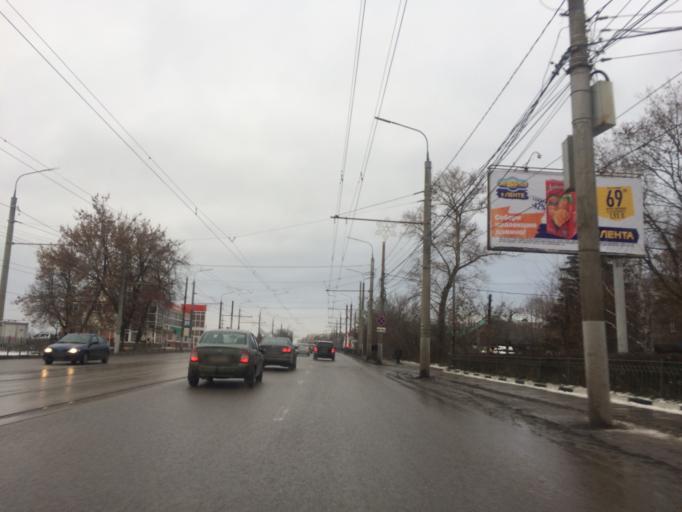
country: RU
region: Tula
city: Tula
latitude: 54.1920
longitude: 37.6285
